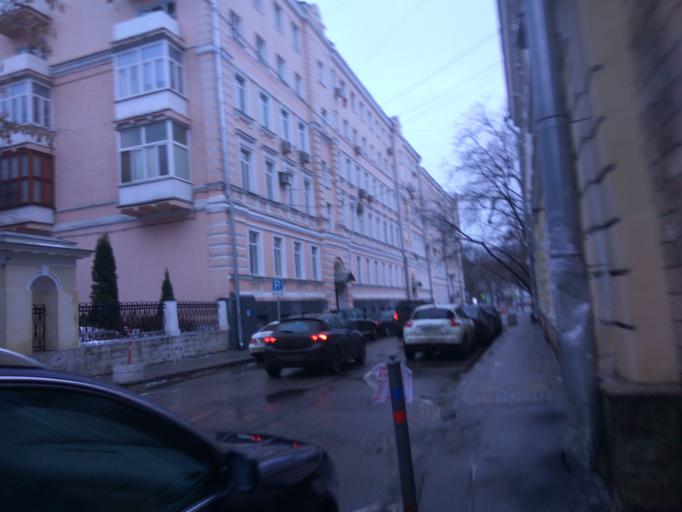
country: RU
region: Moscow
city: Moscow
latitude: 55.7593
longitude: 37.5926
